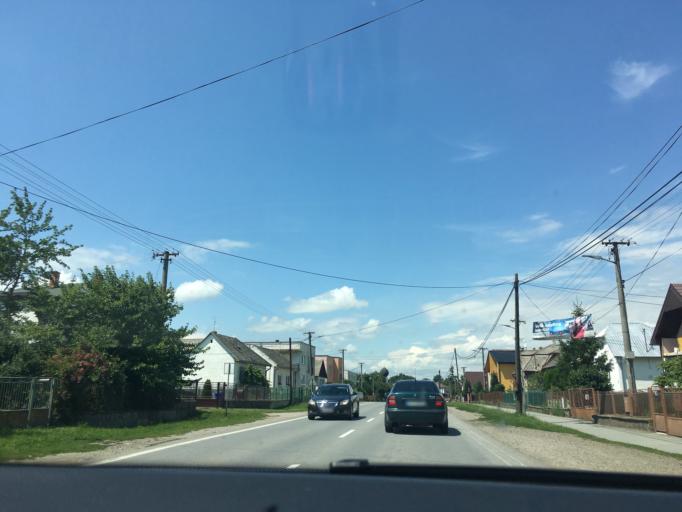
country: SK
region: Kosicky
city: Secovce
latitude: 48.7821
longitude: 21.6840
